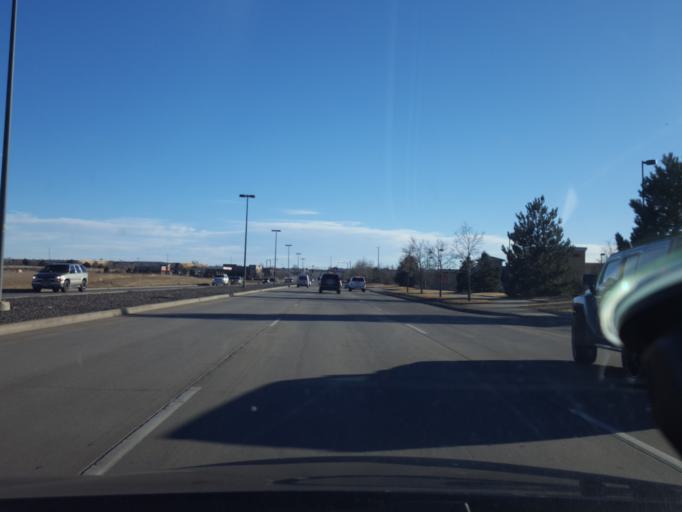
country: US
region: Colorado
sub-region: Adams County
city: Aurora
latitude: 39.7676
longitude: -104.7723
